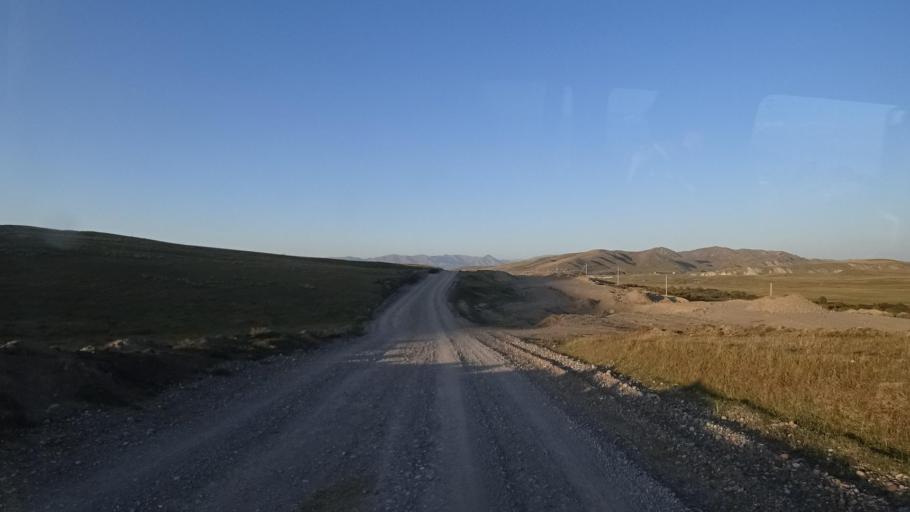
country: KZ
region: Almaty Oblysy
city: Kegen
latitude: 42.8478
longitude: 79.2297
